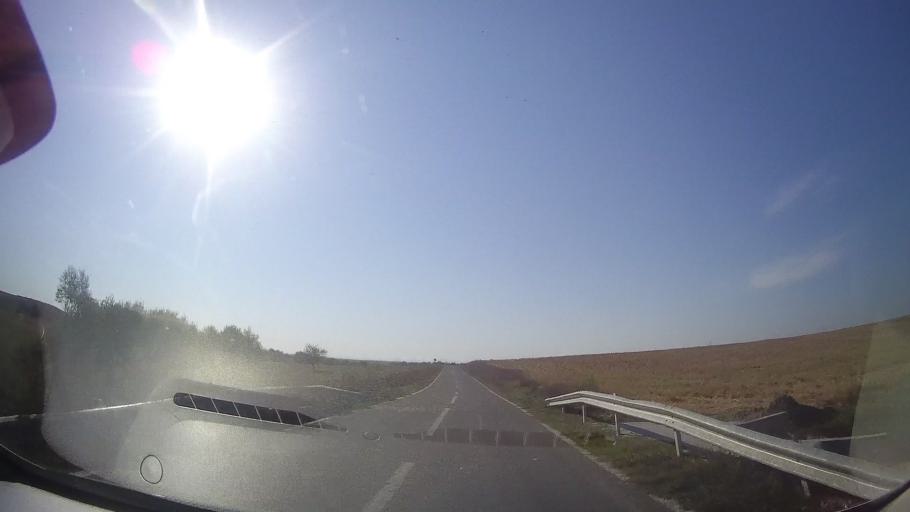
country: RO
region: Timis
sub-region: Comuna Topolovatu Mare
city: Topolovatu Mare
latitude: 45.8013
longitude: 21.5859
